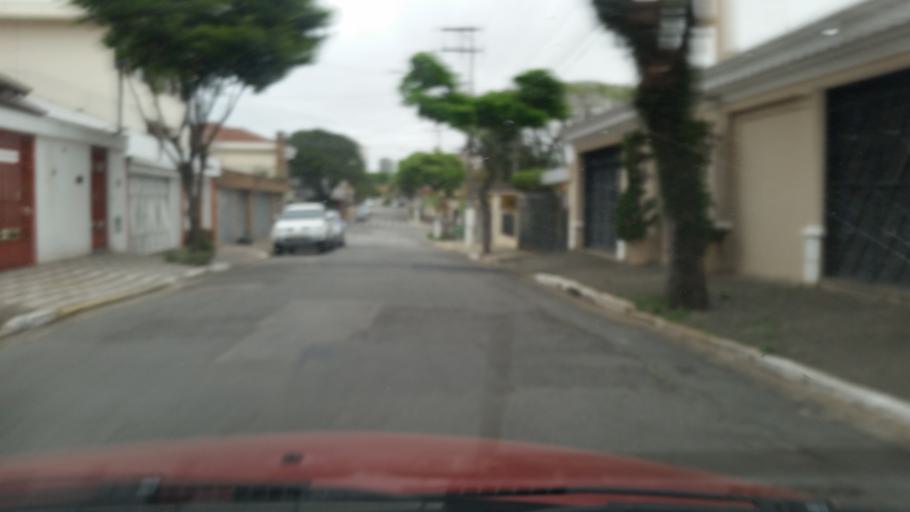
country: BR
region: Sao Paulo
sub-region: Sao Caetano Do Sul
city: Sao Caetano do Sul
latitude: -23.6154
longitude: -46.6197
